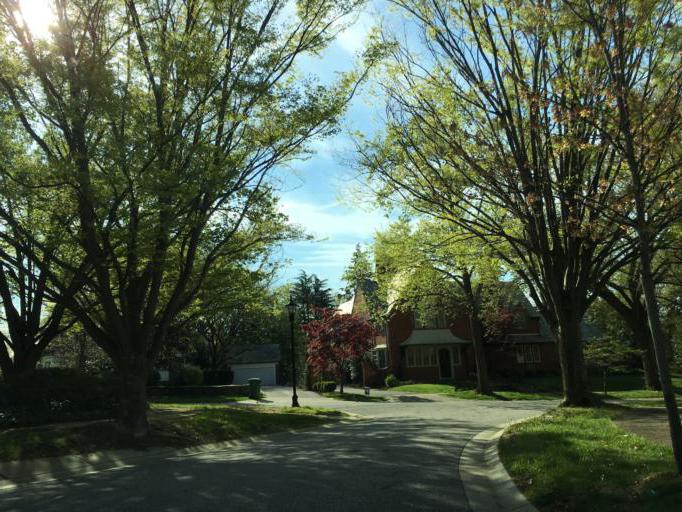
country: US
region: Maryland
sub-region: City of Baltimore
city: Baltimore
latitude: 39.3449
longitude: -76.6194
